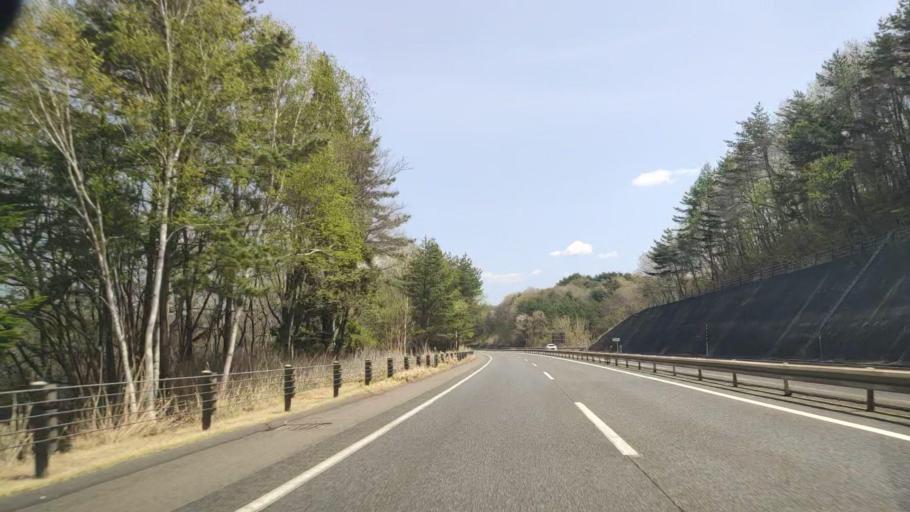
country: JP
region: Iwate
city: Ichinohe
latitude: 40.3154
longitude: 141.4388
